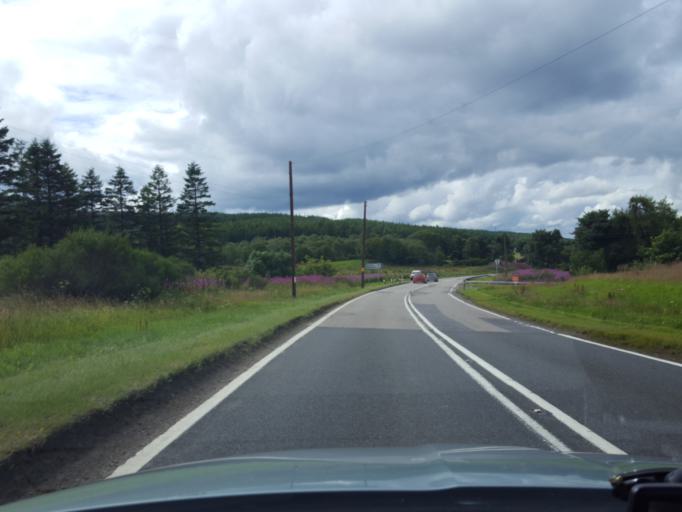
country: GB
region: Scotland
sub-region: Moray
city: Rothes
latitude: 57.4496
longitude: -3.2584
